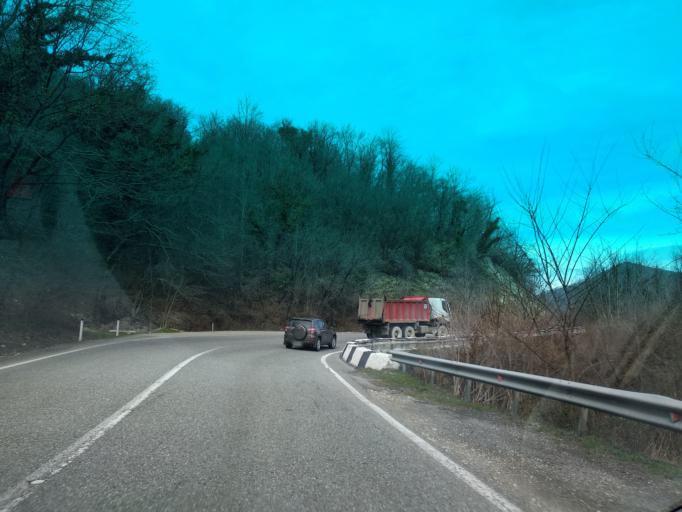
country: RU
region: Krasnodarskiy
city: Shepsi
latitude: 44.0598
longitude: 39.1329
